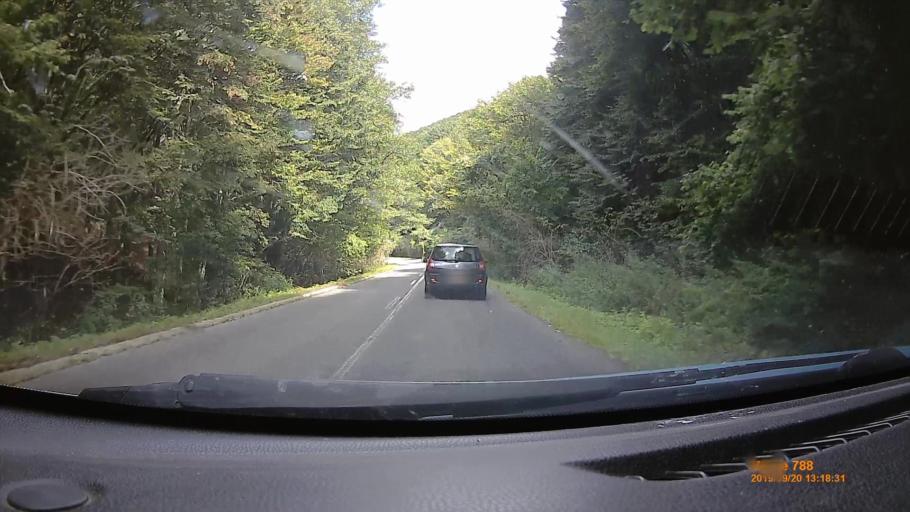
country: HU
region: Heves
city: Felsotarkany
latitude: 48.0013
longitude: 20.4633
